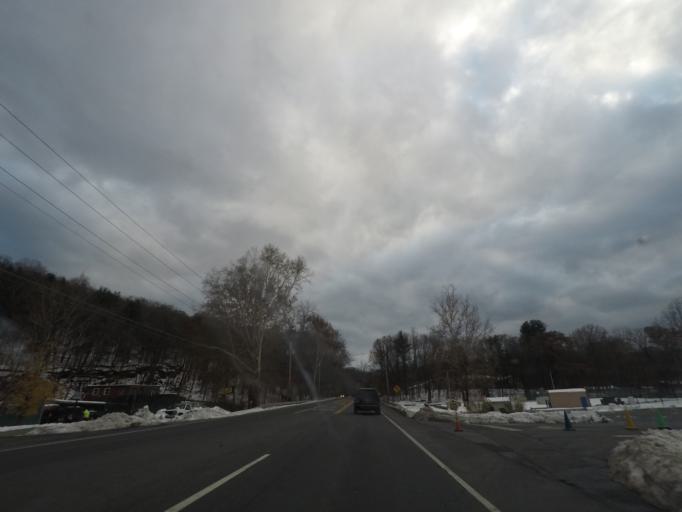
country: US
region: New York
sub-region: Ulster County
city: Rosendale Village
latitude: 41.8425
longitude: -74.0745
